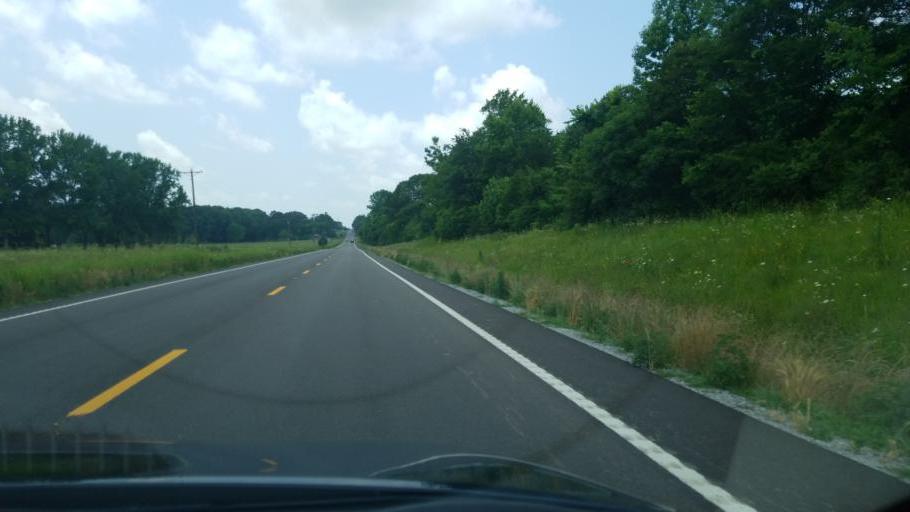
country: US
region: Tennessee
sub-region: Carroll County
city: Huntingdon
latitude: 36.0263
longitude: -88.3630
